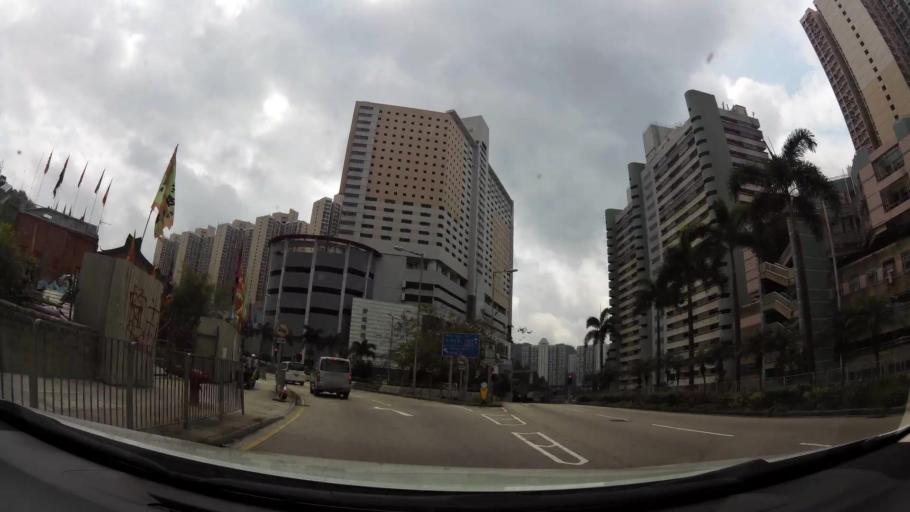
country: HK
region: Kowloon City
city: Kowloon
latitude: 22.3186
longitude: 114.2350
